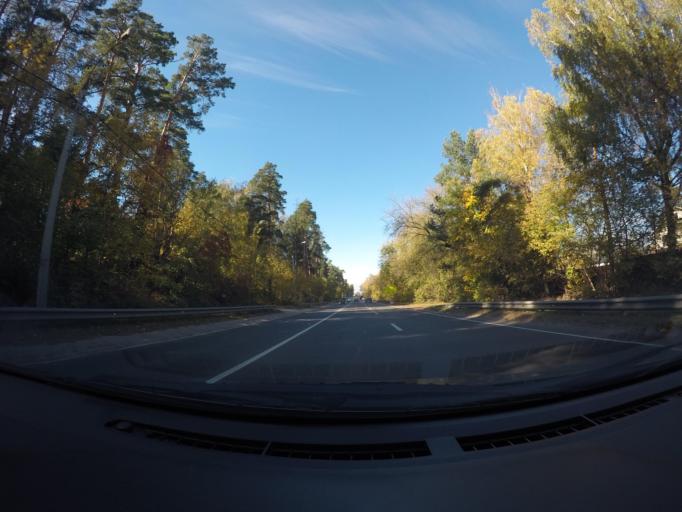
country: RU
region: Moskovskaya
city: Udel'naya
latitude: 55.6288
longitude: 37.9921
